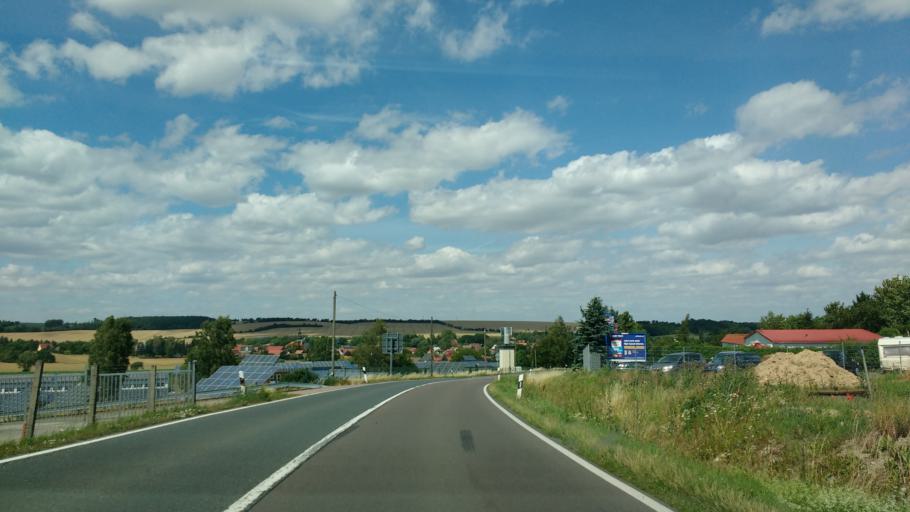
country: DE
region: Saxony-Anhalt
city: Farnstadt
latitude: 51.4200
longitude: 11.5675
